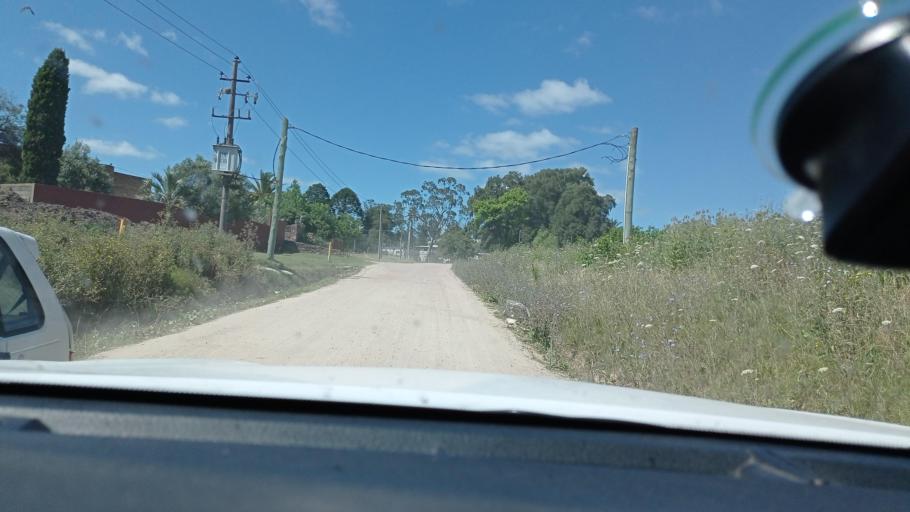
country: UY
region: Canelones
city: Pando
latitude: -34.7318
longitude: -55.9757
